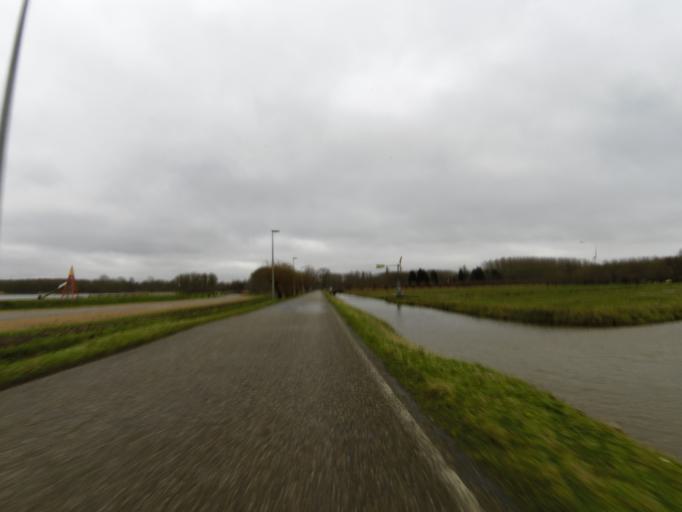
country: NL
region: South Holland
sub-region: Gemeente Vlaardingen
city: Vlaardingen
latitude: 51.9124
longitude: 4.2956
